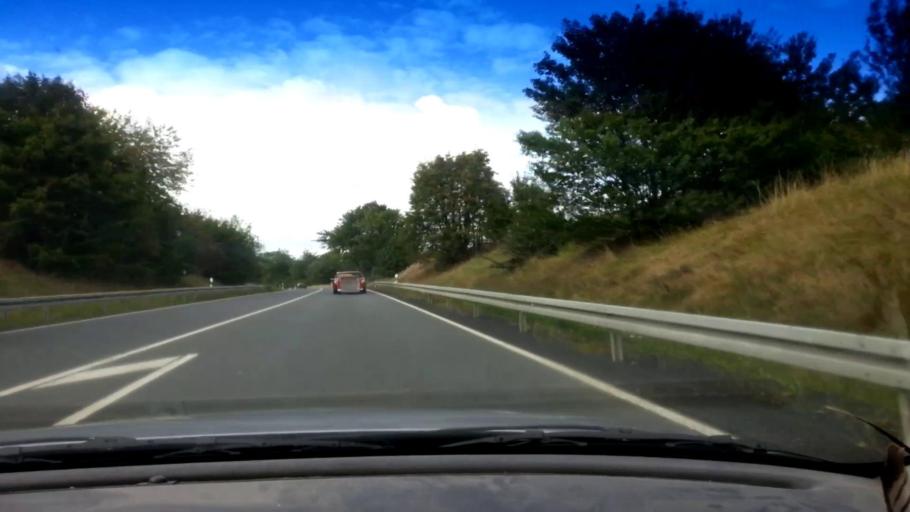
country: DE
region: Bavaria
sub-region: Upper Franconia
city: Marktredwitz
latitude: 50.0094
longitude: 12.1064
